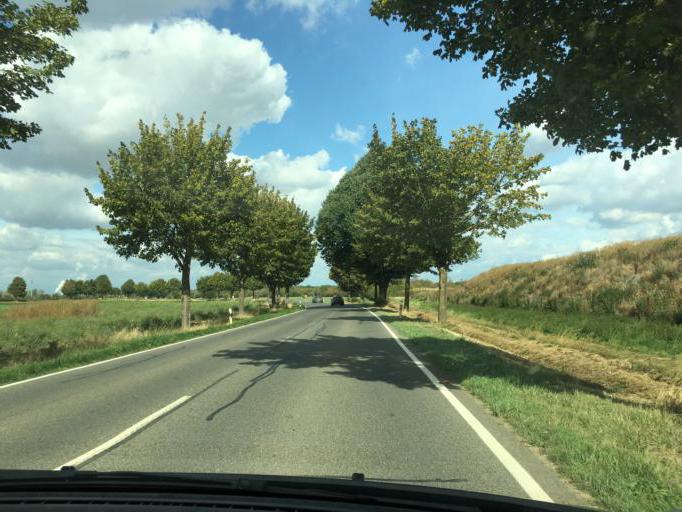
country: DE
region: North Rhine-Westphalia
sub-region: Regierungsbezirk Koln
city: Elsdorf
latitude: 50.8826
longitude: 6.6065
